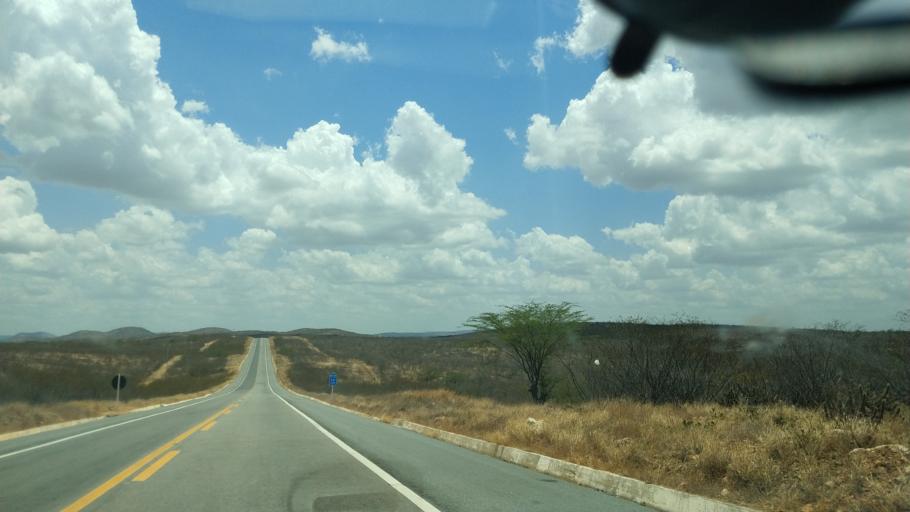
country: BR
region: Rio Grande do Norte
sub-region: Currais Novos
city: Currais Novos
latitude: -6.2452
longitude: -36.4679
